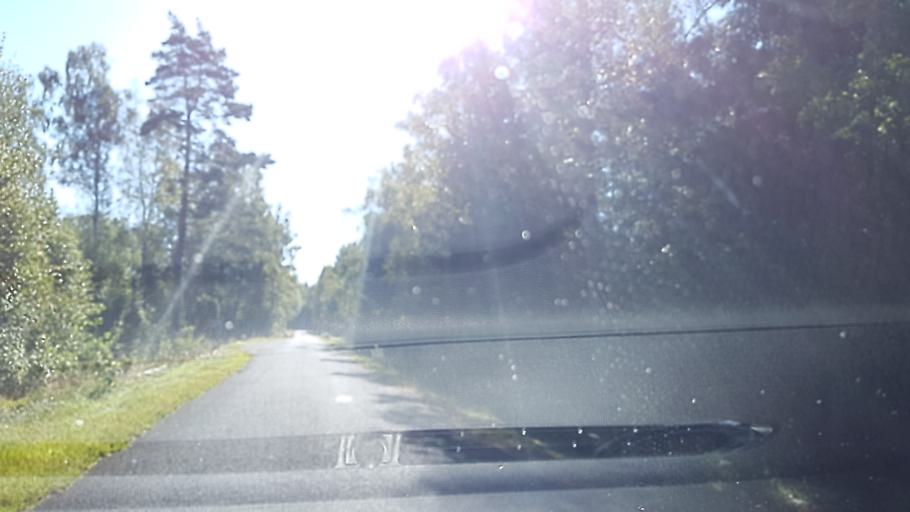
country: SE
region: Kronoberg
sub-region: Ljungby Kommun
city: Ljungby
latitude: 56.8052
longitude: 14.0299
